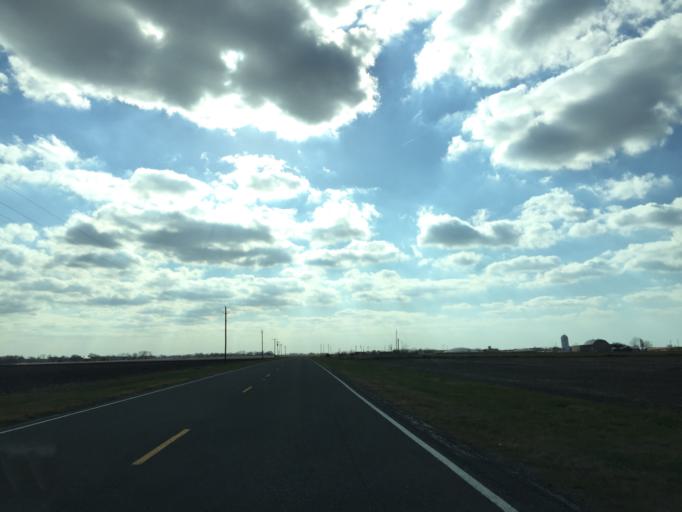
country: US
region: Texas
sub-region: Williamson County
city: Granger
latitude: 30.6577
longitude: -97.3757
